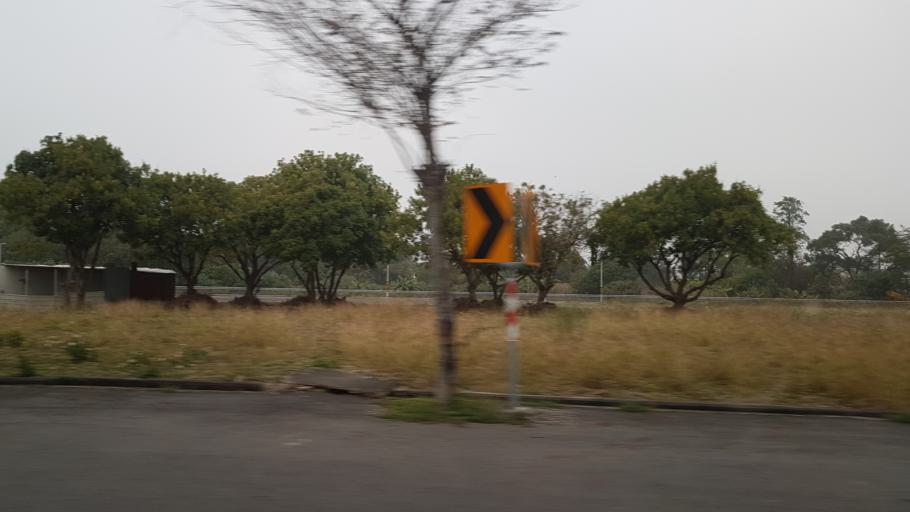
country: TW
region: Taiwan
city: Xinying
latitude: 23.3320
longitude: 120.3174
